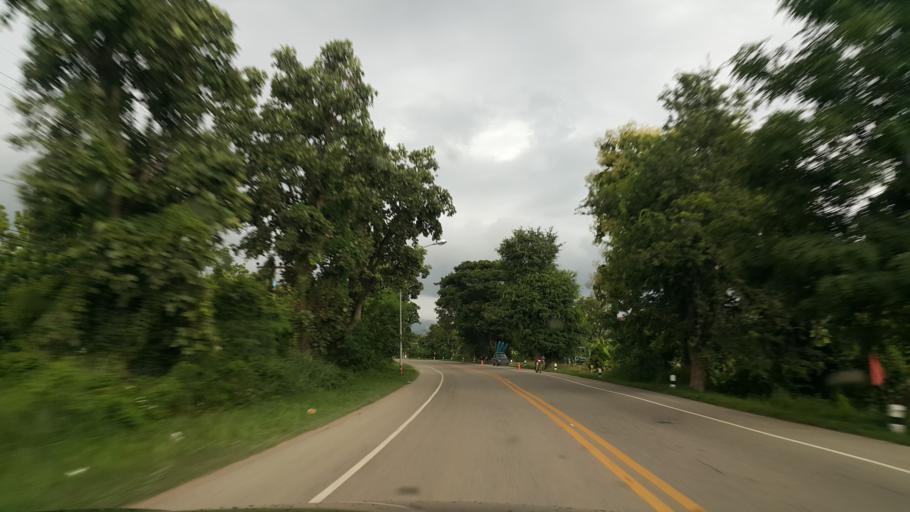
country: TH
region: Phayao
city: Dok Kham Tai
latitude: 19.2296
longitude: 100.0482
